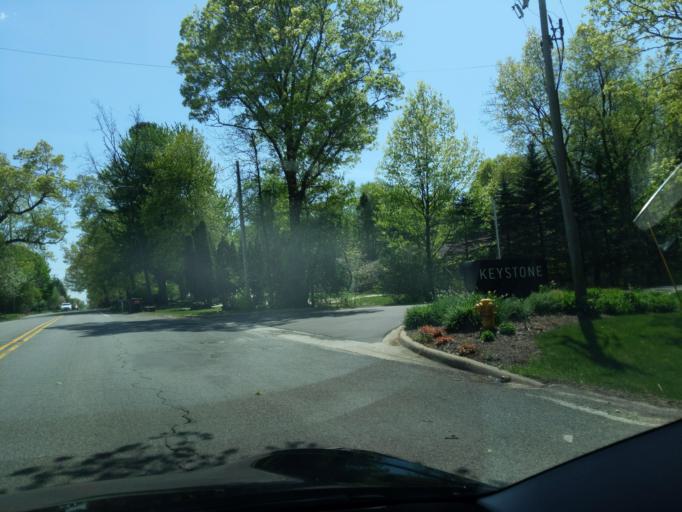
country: US
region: Michigan
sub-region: Kent County
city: Forest Hills
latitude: 42.9519
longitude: -85.5403
